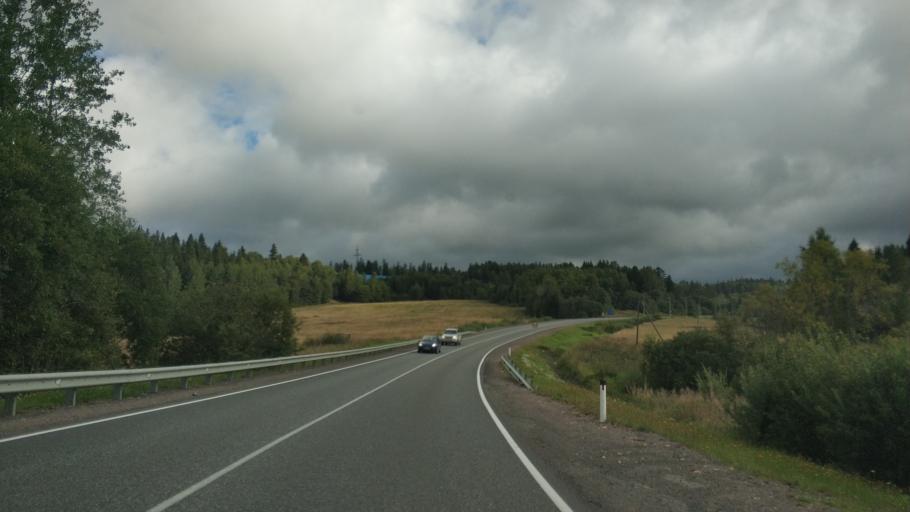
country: RU
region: Republic of Karelia
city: Khelyulya
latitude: 61.7717
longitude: 30.6550
